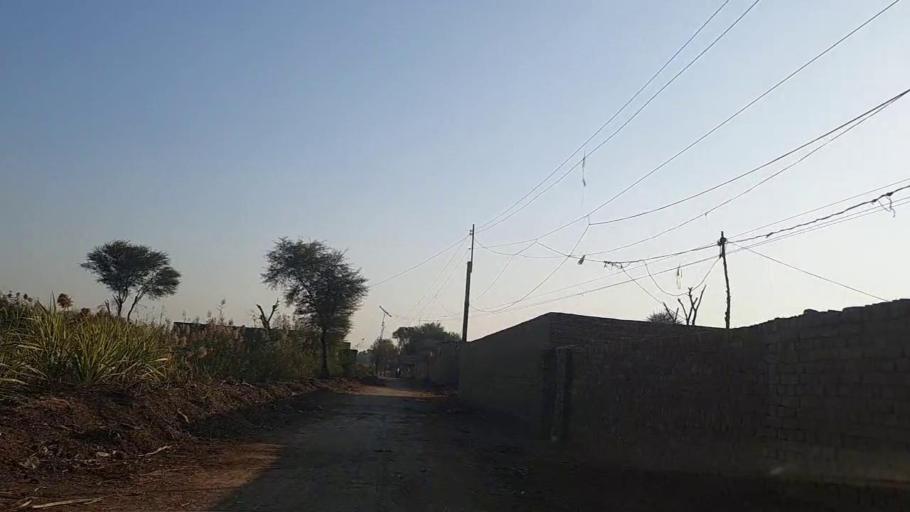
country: PK
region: Sindh
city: Sakrand
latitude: 26.3062
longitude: 68.1432
